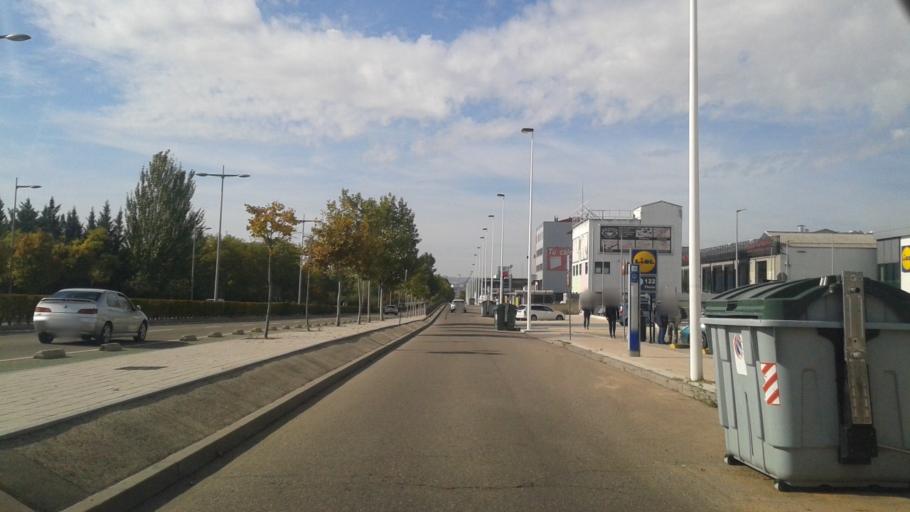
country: ES
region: Castille and Leon
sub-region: Provincia de Valladolid
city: Zaratan
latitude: 41.6274
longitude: -4.7598
